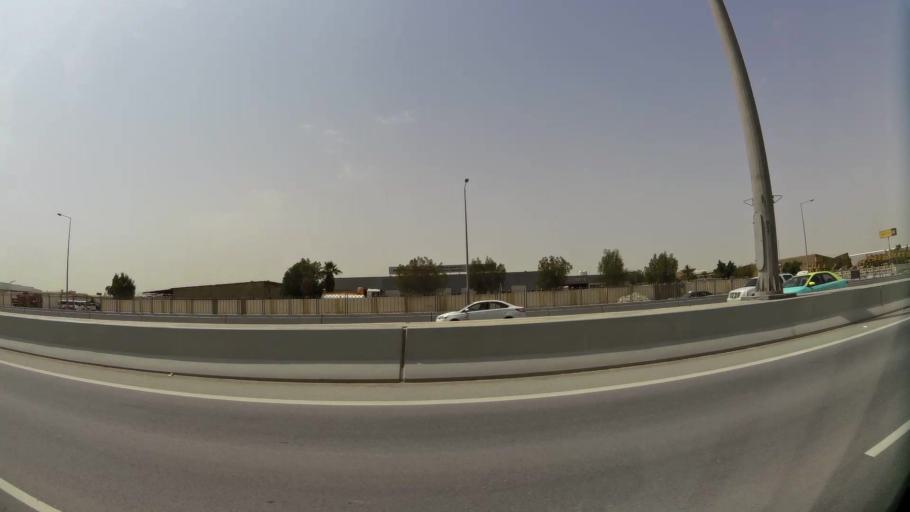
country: QA
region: Baladiyat ar Rayyan
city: Ar Rayyan
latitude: 25.2087
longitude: 51.4439
